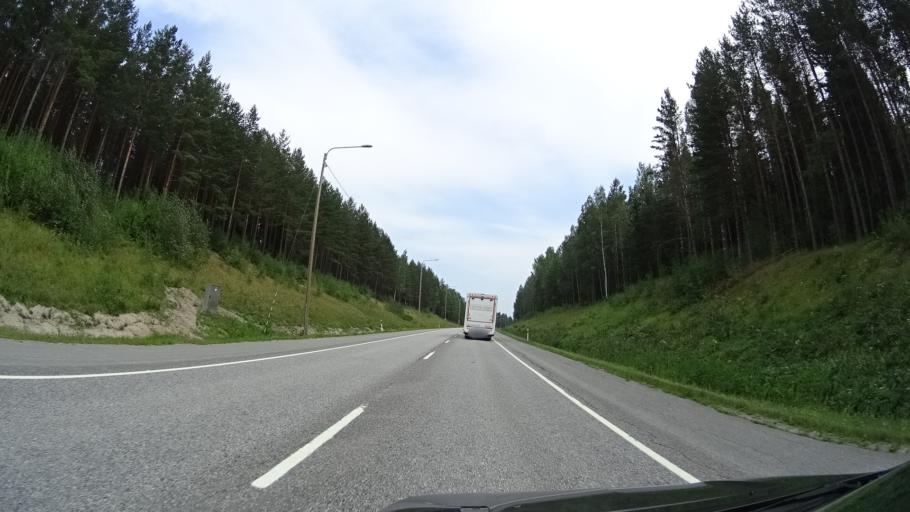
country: FI
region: Uusimaa
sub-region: Raaseporin
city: Karis
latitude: 60.0678
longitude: 23.8066
